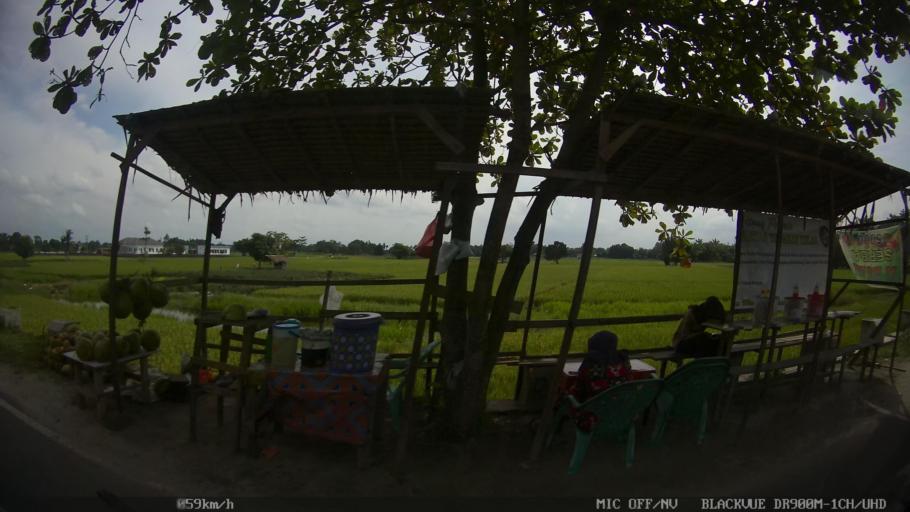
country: ID
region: North Sumatra
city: Percut
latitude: 3.6126
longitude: 98.8450
